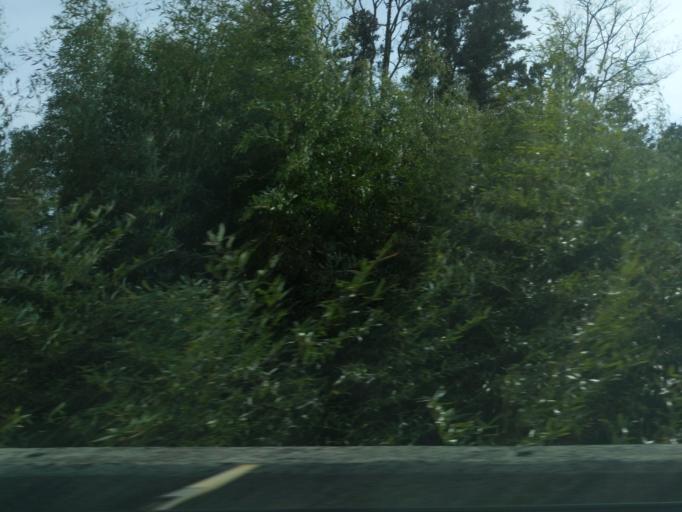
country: JP
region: Miyagi
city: Furukawa
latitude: 38.6366
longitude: 141.0081
